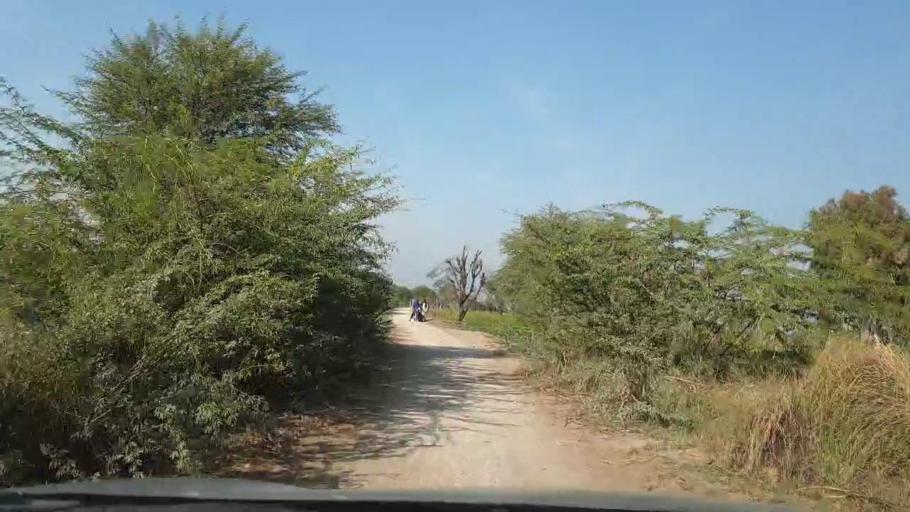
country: PK
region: Sindh
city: Berani
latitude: 25.7233
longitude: 68.7615
